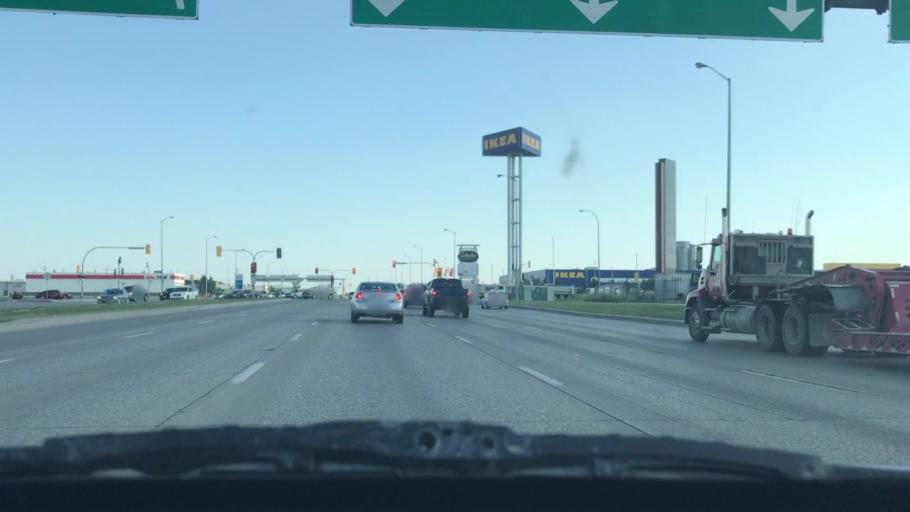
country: CA
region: Manitoba
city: Winnipeg
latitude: 49.8430
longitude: -97.2088
